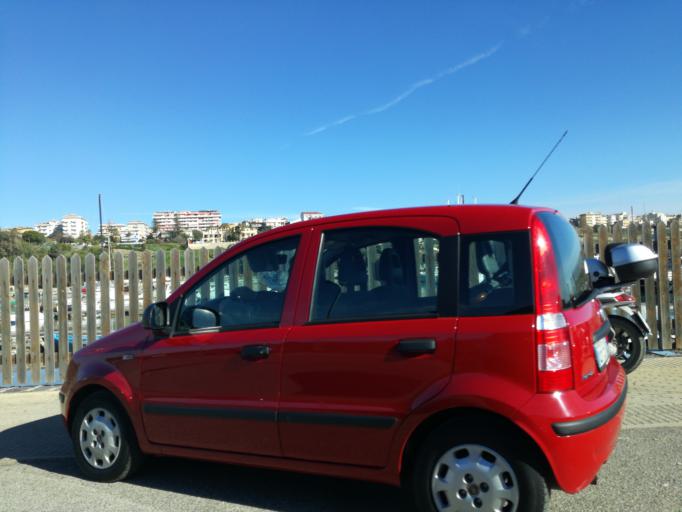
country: IT
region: Sicily
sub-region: Provincia di Caltanissetta
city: Gela
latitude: 37.0652
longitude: 14.2312
